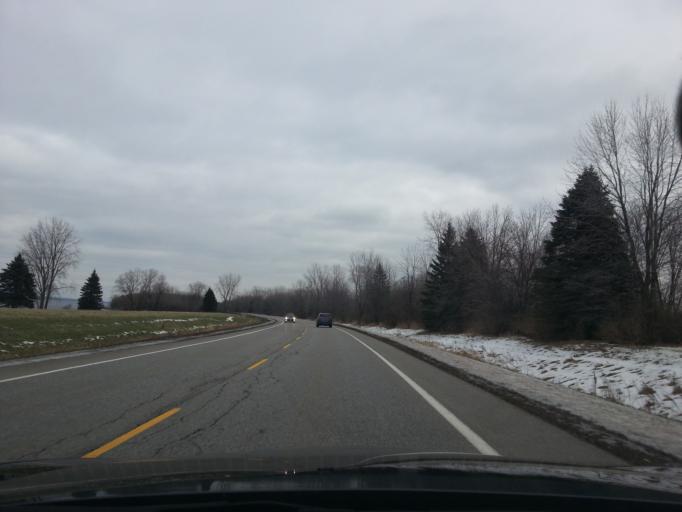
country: CA
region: Quebec
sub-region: Outaouais
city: Gatineau
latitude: 45.4647
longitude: -75.5921
